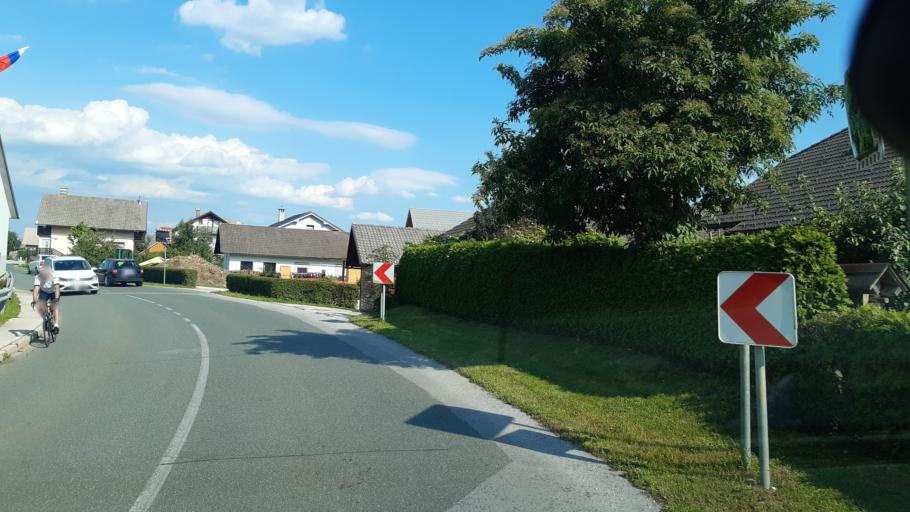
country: SI
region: Sencur
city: Hrastje
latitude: 46.2148
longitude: 14.3881
